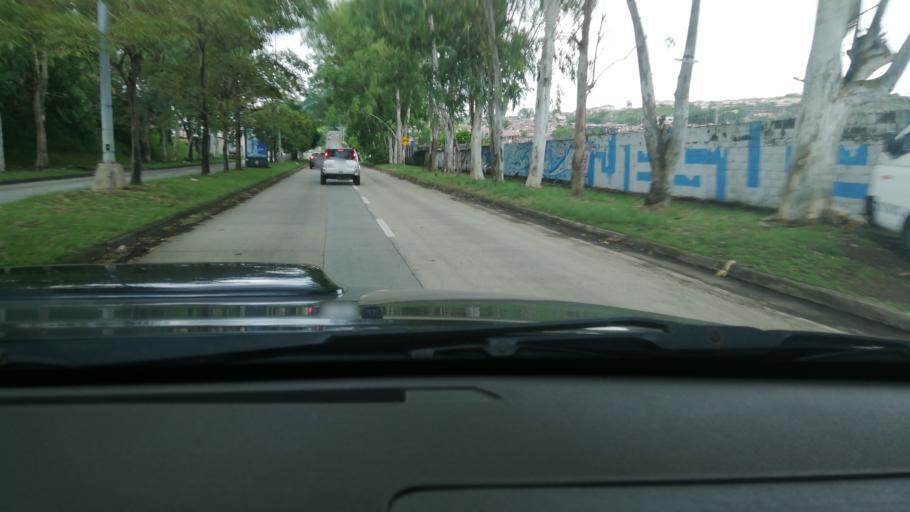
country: PA
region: Panama
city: San Miguelito
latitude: 9.0446
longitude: -79.4821
